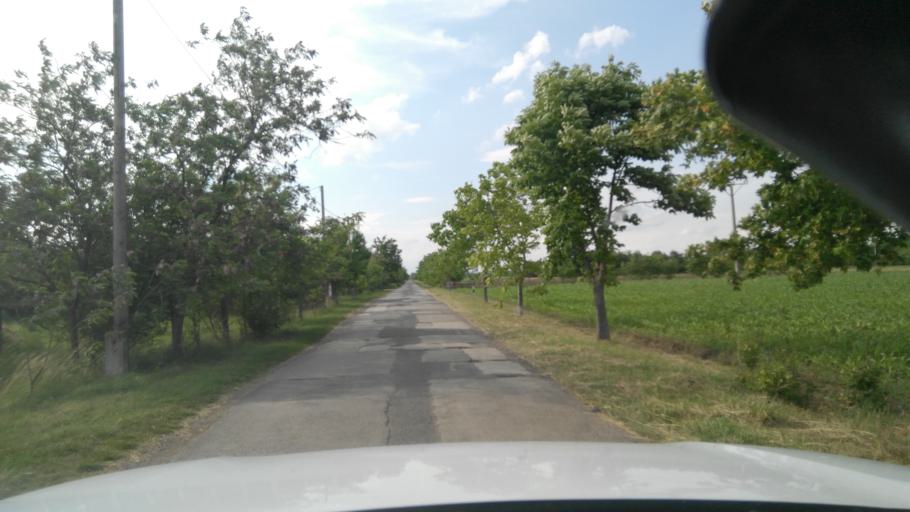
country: HU
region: Bekes
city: Bekescsaba
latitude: 46.7080
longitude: 21.1549
